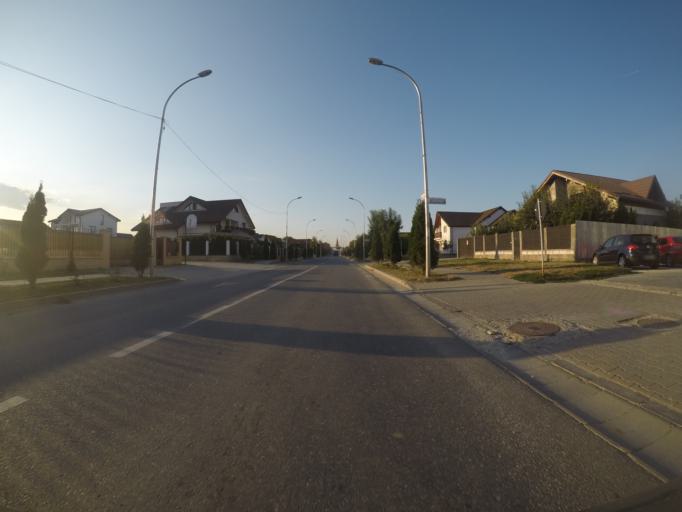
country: RO
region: Sibiu
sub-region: Comuna Selimbar
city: Selimbar
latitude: 45.7619
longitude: 24.1973
